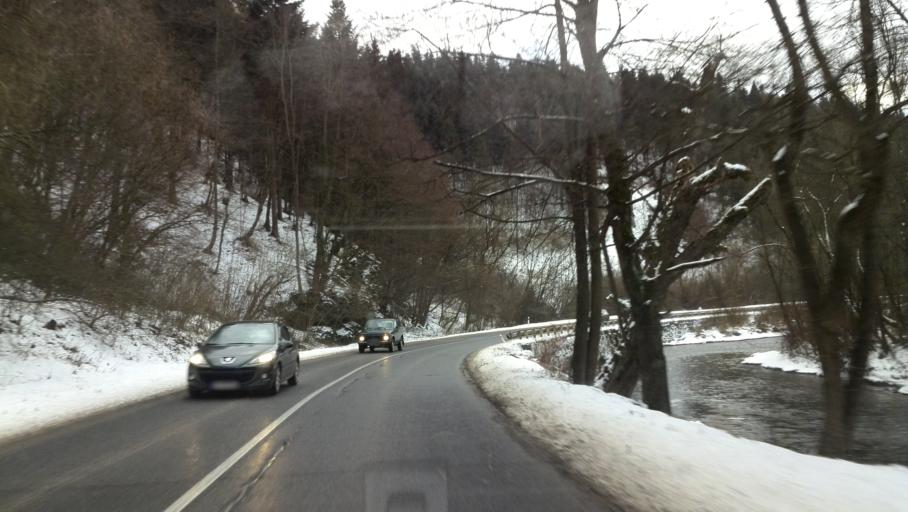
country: SK
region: Kosicky
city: Gelnica
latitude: 48.8674
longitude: 20.9757
